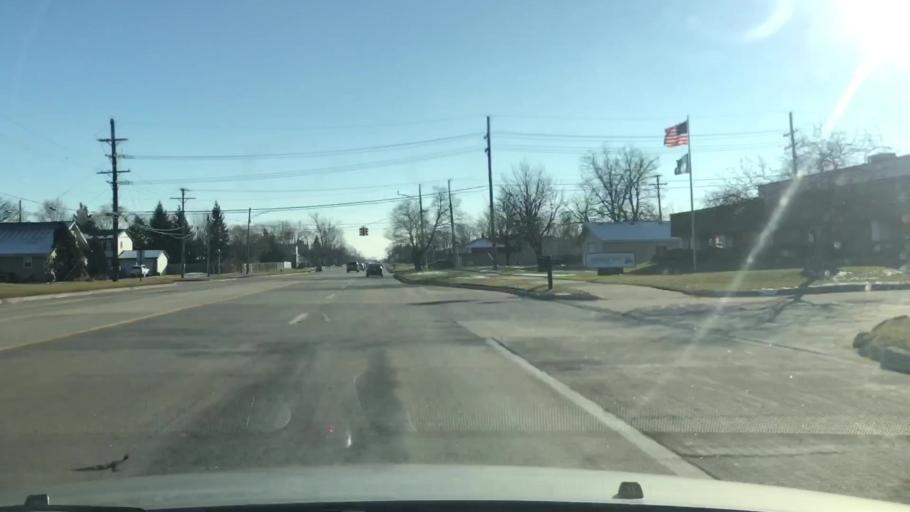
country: US
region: Michigan
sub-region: Oakland County
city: Clawson
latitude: 42.5565
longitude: -83.1081
